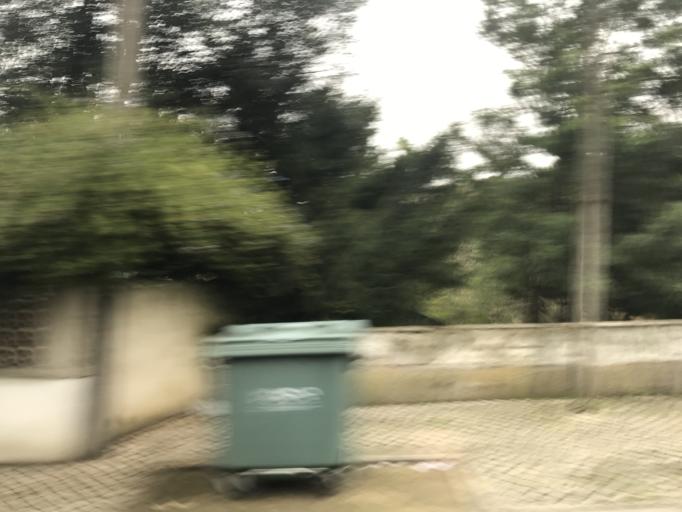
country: PT
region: Lisbon
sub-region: Sintra
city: Sintra
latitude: 38.7936
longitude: -9.3741
